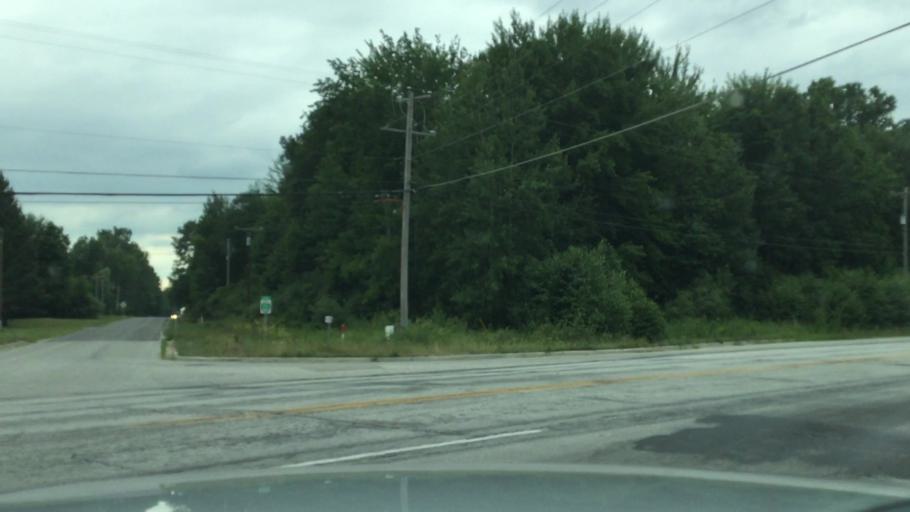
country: US
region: Michigan
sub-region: Saginaw County
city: Birch Run
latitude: 43.3072
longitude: -83.8124
